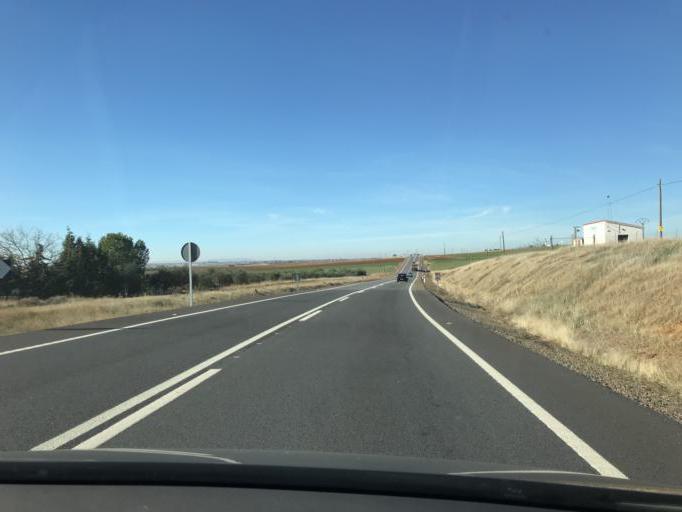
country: ES
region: Extremadura
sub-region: Provincia de Badajoz
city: Granja de Torrehermosa
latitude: 38.2979
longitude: -5.6295
